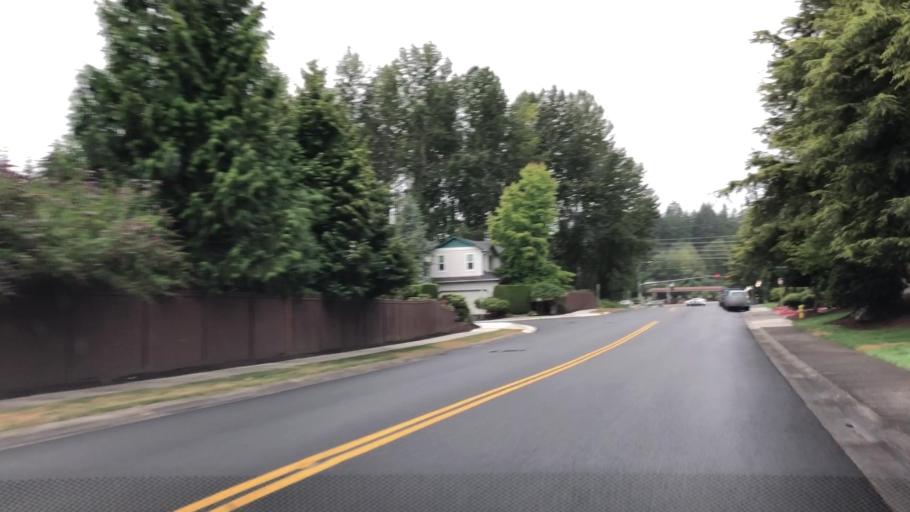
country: US
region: Washington
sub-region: Snohomish County
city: North Creek
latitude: 47.8284
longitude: -122.2062
